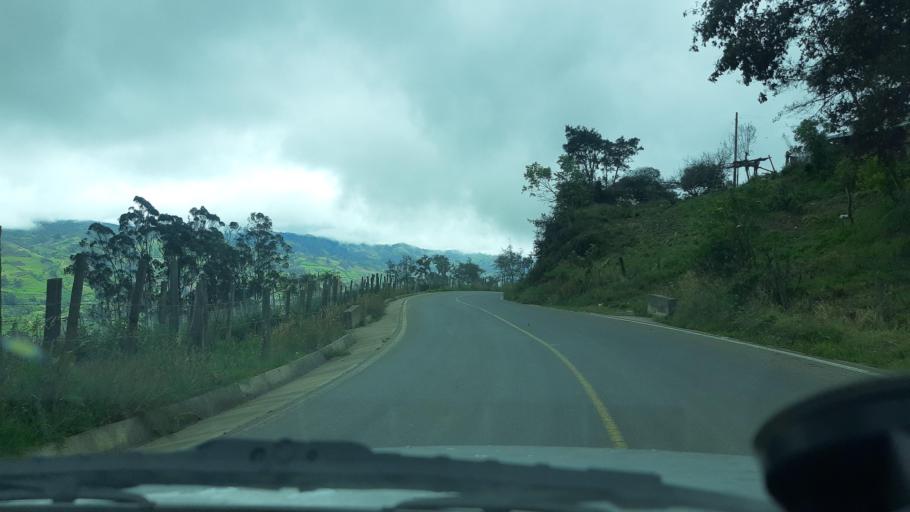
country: CO
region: Cundinamarca
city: Umbita
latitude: 5.2351
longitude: -73.4671
